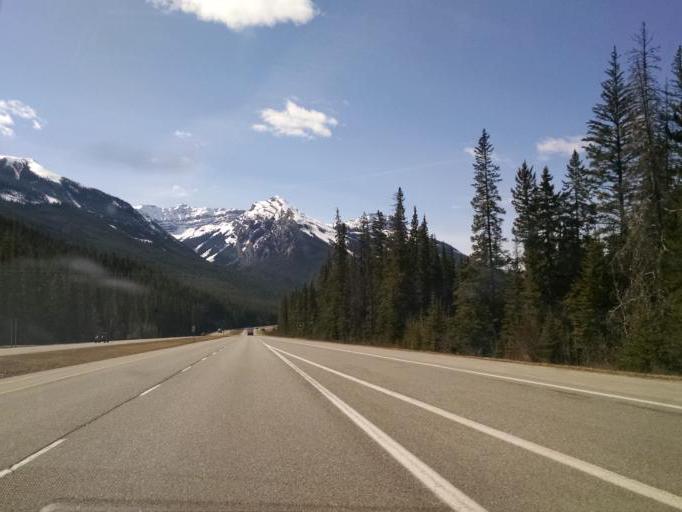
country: CA
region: Alberta
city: Banff
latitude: 51.1575
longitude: -115.6900
